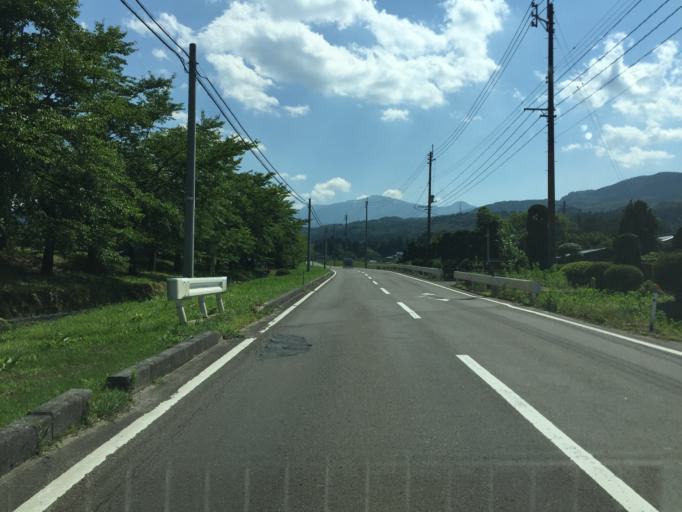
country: JP
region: Fukushima
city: Fukushima-shi
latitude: 37.7194
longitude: 140.3557
